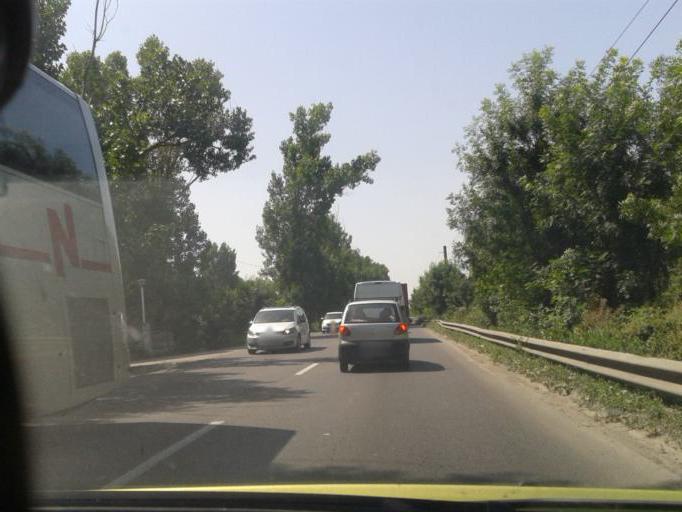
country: RO
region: Ilfov
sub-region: Comuna Pantelimon
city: Pantelimon
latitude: 44.4484
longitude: 26.2357
